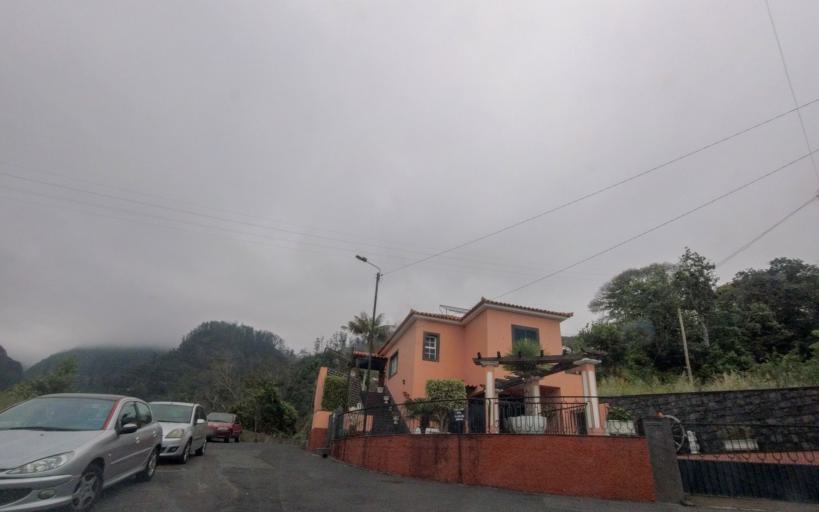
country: PT
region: Madeira
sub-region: Funchal
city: Nossa Senhora do Monte
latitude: 32.6796
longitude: -16.9142
